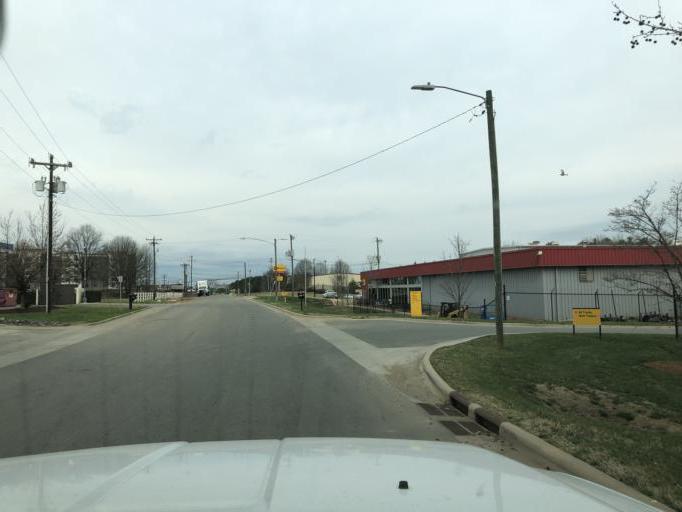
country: US
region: North Carolina
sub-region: Mecklenburg County
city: Huntersville
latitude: 35.3460
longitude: -80.8388
